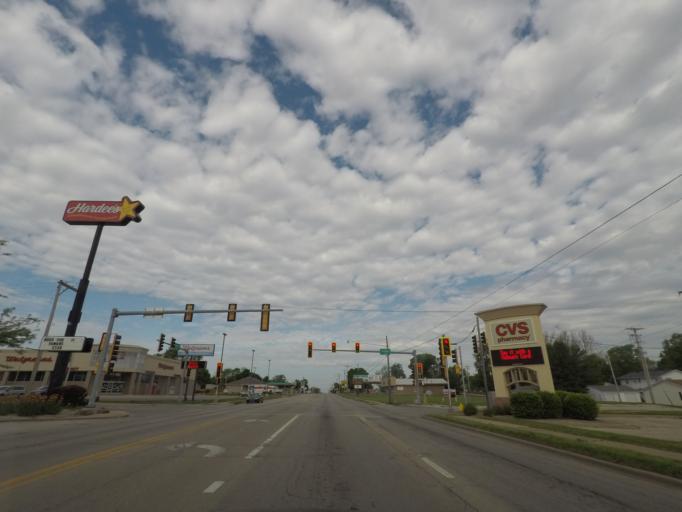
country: US
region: Illinois
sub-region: Logan County
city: Lincoln
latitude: 40.1577
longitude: -89.3746
